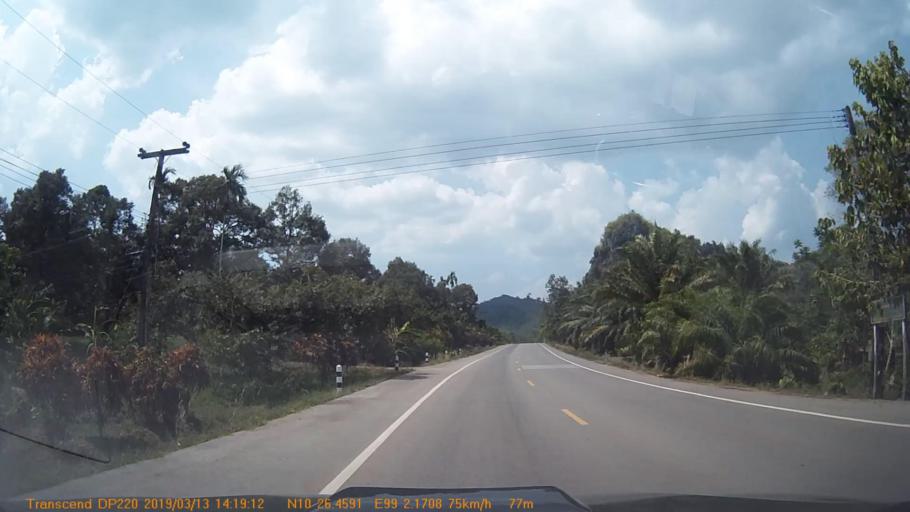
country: TH
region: Chumphon
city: Chumphon
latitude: 10.4293
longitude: 99.0400
